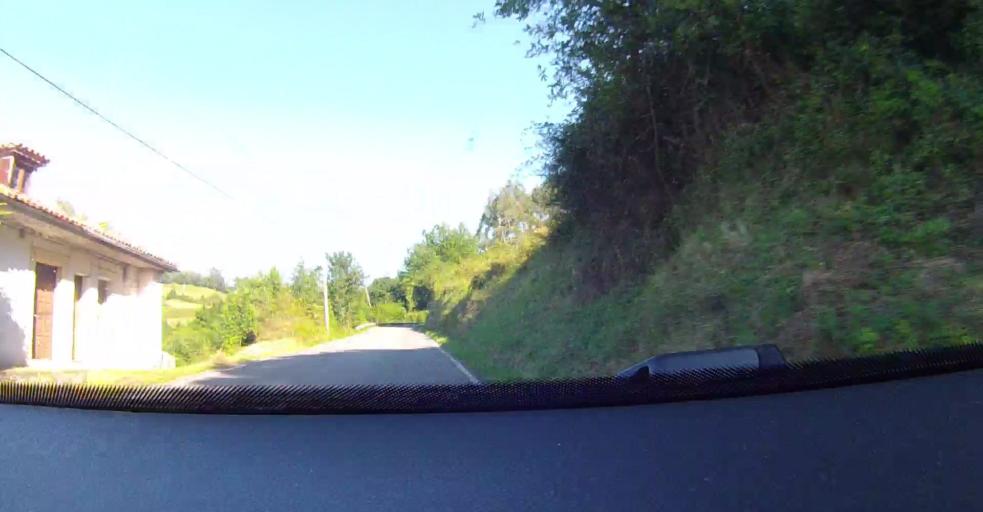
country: ES
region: Asturias
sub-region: Province of Asturias
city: Villaviciosa
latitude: 43.4859
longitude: -5.4111
